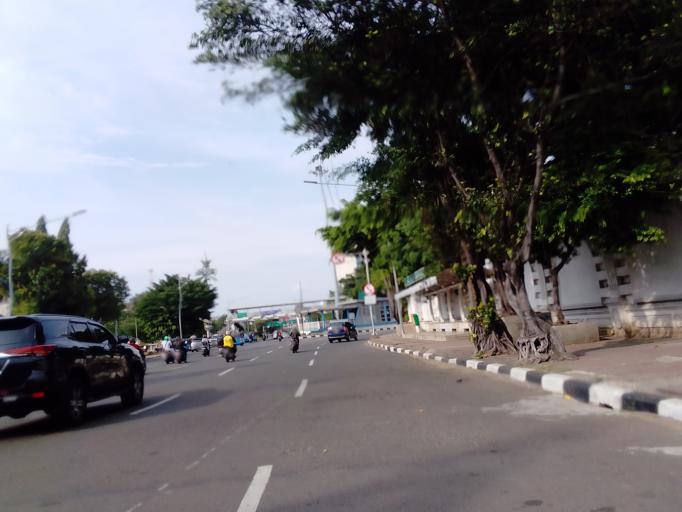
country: ID
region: Jakarta Raya
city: Jakarta
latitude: -6.1664
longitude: 106.8341
